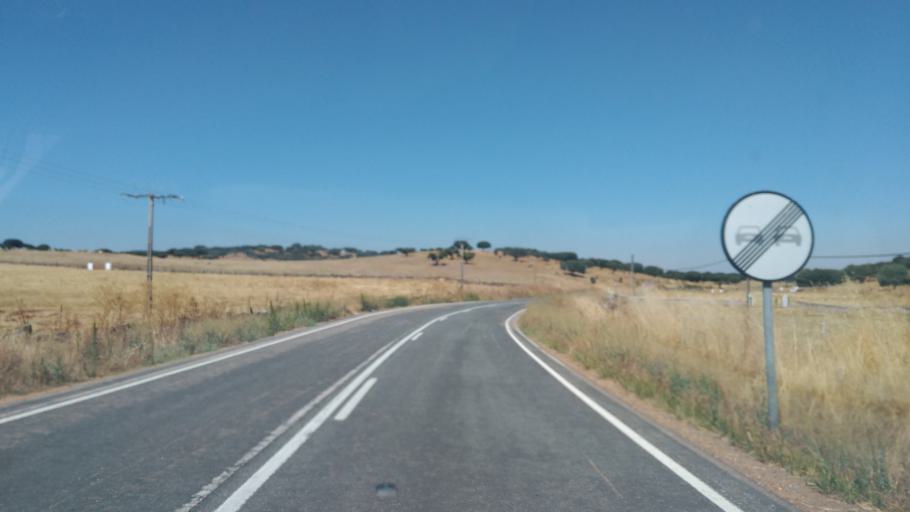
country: ES
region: Castille and Leon
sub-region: Provincia de Salamanca
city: Matilla de los Canos del Rio
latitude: 40.7969
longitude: -5.9189
